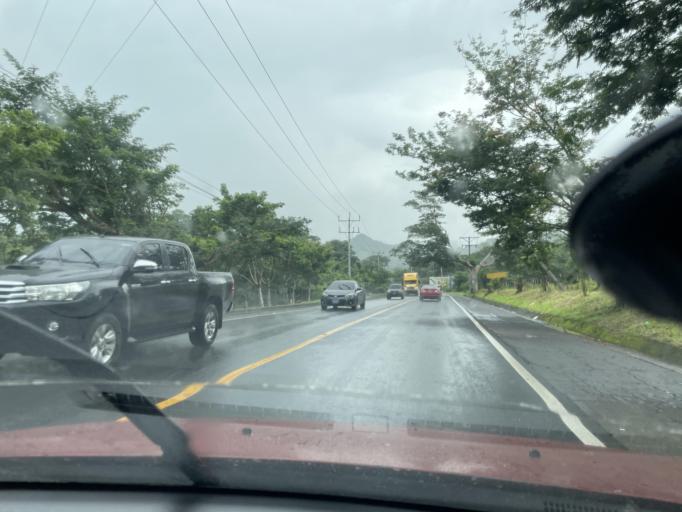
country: SV
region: San Miguel
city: San Miguel
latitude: 13.5418
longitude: -88.1284
